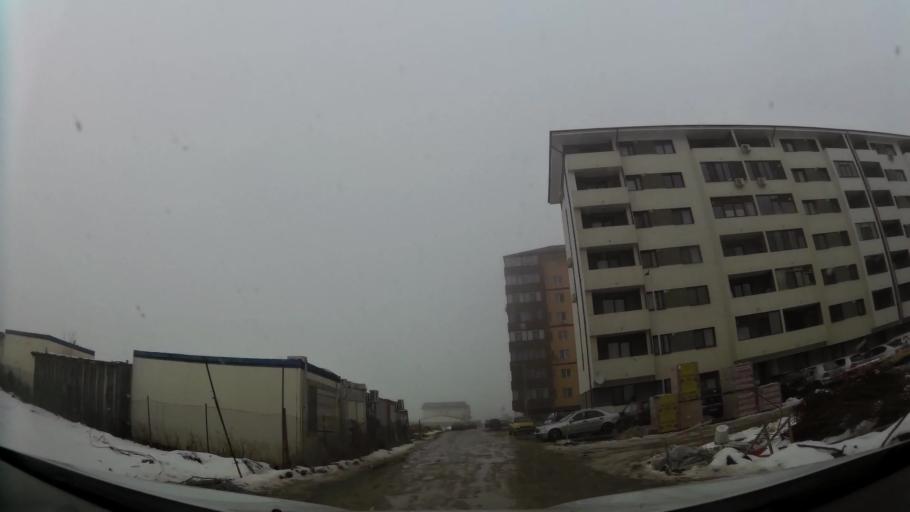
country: RO
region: Ilfov
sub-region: Comuna Chiajna
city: Chiajna
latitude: 44.4465
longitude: 25.9761
